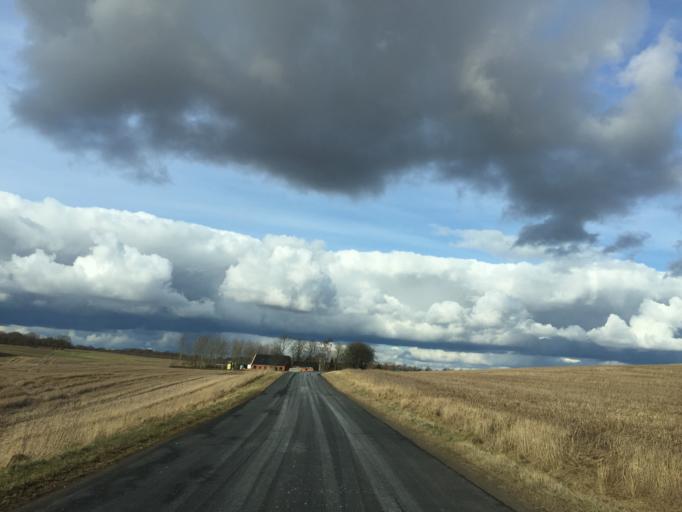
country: DK
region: Central Jutland
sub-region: Favrskov Kommune
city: Hammel
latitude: 56.1983
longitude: 9.8110
